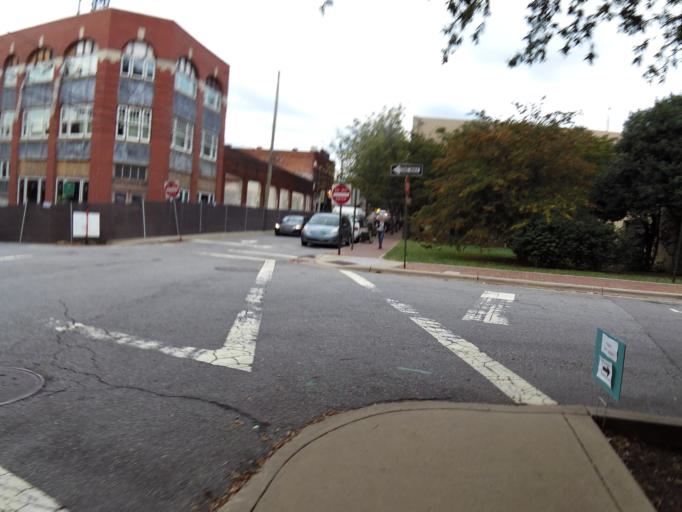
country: US
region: North Carolina
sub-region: Buncombe County
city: Asheville
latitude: 35.5941
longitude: -82.5501
